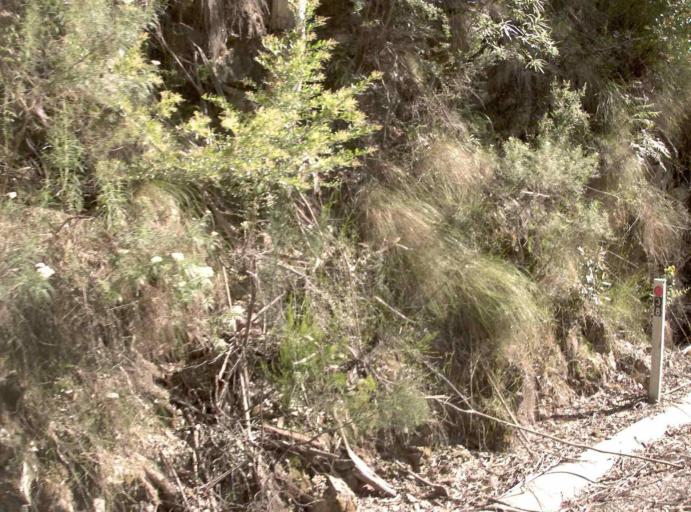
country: AU
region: Victoria
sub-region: East Gippsland
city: Lakes Entrance
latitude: -37.5021
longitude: 148.5487
